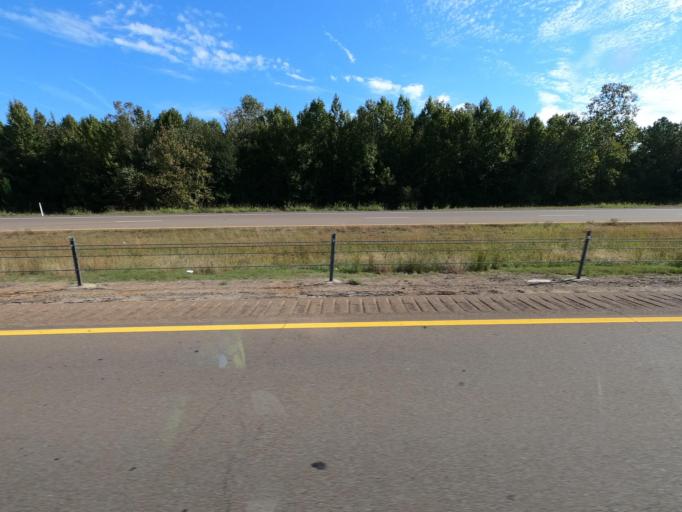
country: US
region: Tennessee
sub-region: Shelby County
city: Arlington
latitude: 35.2833
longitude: -89.6818
